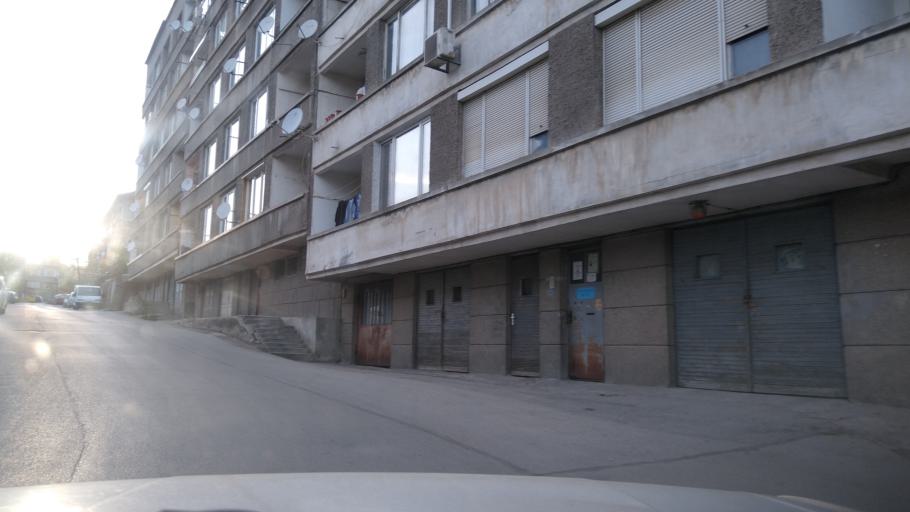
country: BG
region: Gabrovo
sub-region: Obshtina Gabrovo
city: Gabrovo
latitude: 42.8621
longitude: 25.3272
